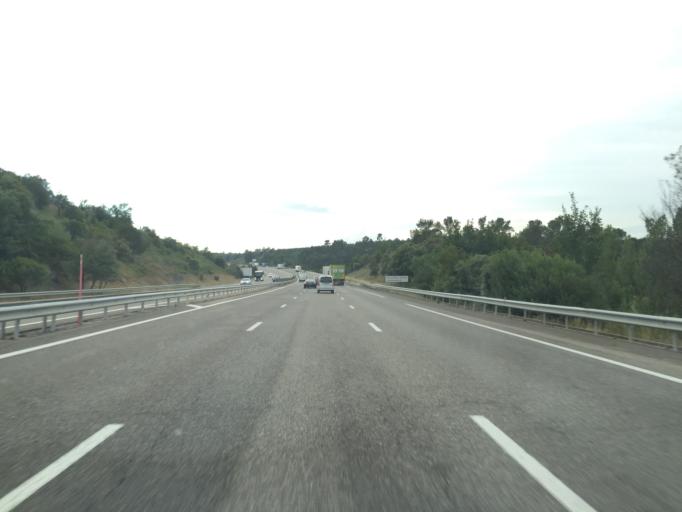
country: FR
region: Provence-Alpes-Cote d'Azur
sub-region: Departement du Var
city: Tourves
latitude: 43.4403
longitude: 5.9056
